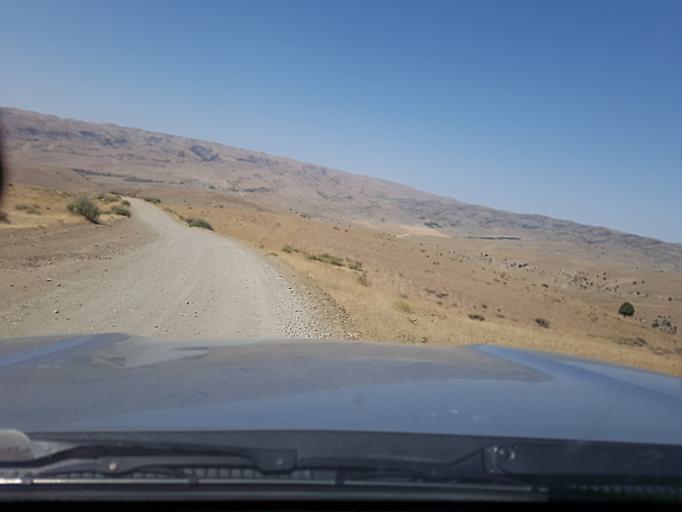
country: TM
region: Ahal
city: Baharly
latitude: 38.3725
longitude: 56.9092
